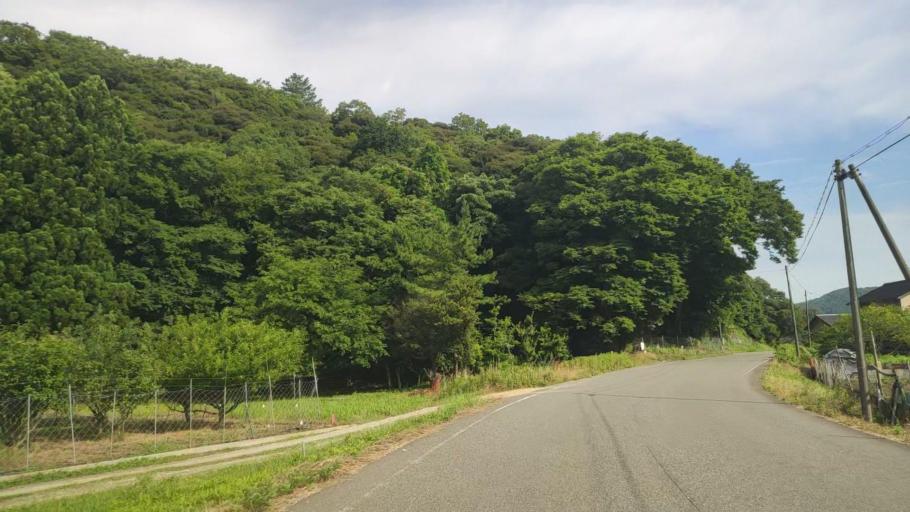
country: JP
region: Hyogo
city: Toyooka
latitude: 35.6348
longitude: 134.8369
